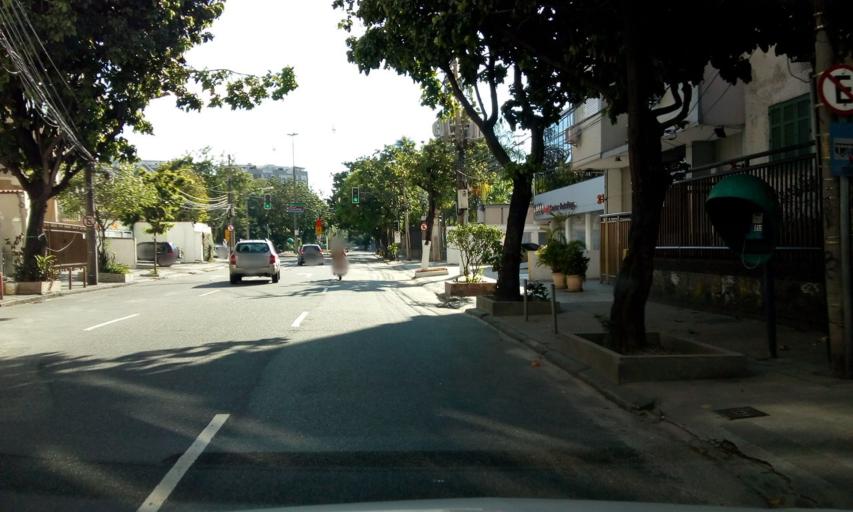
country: BR
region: Rio de Janeiro
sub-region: Rio De Janeiro
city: Rio de Janeiro
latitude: -22.9540
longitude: -43.1805
